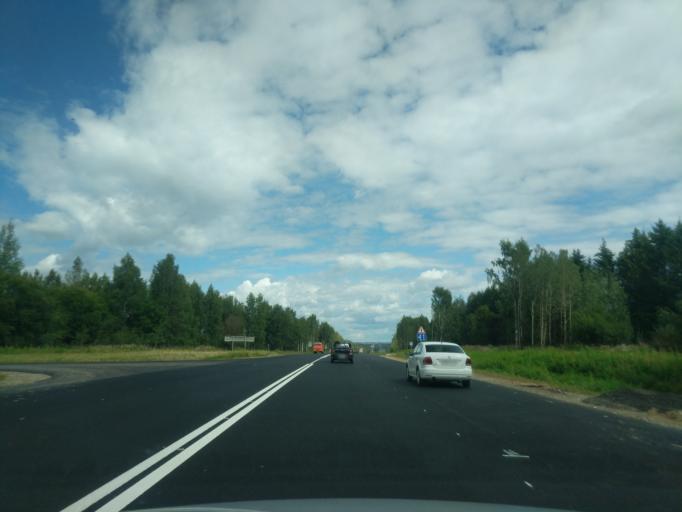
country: RU
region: Kostroma
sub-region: Kostromskoy Rayon
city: Kostroma
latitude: 57.7263
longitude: 40.7961
